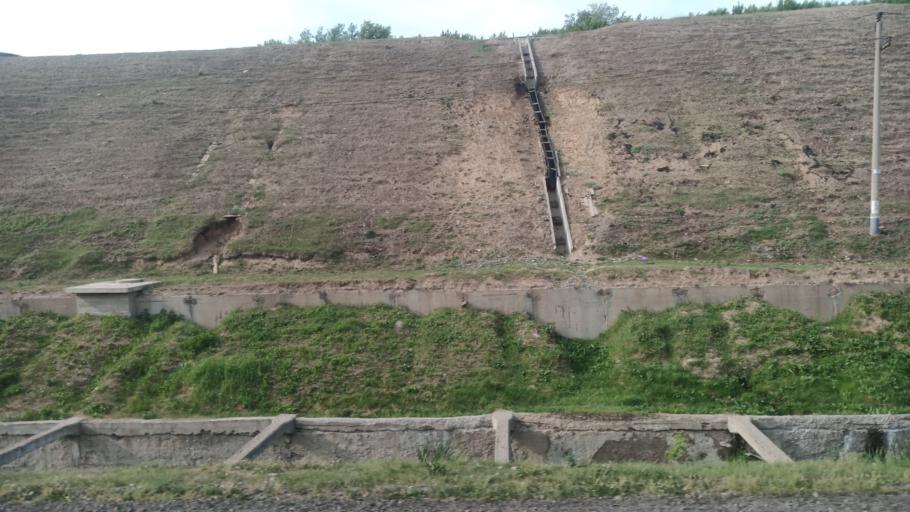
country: RU
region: Altai Krai
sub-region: Gorod Barnaulskiy
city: Barnaul
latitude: 53.3737
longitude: 83.7989
